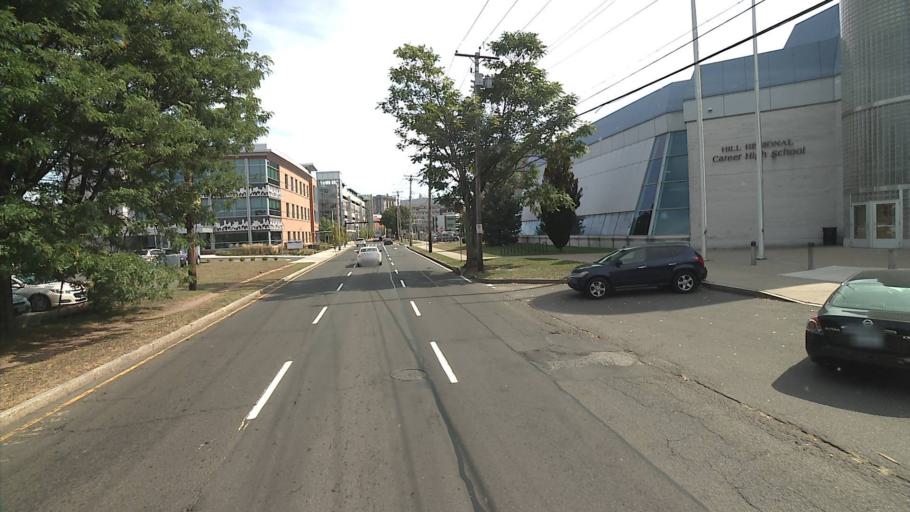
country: US
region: Connecticut
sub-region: New Haven County
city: New Haven
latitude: 41.3061
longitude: -72.9405
